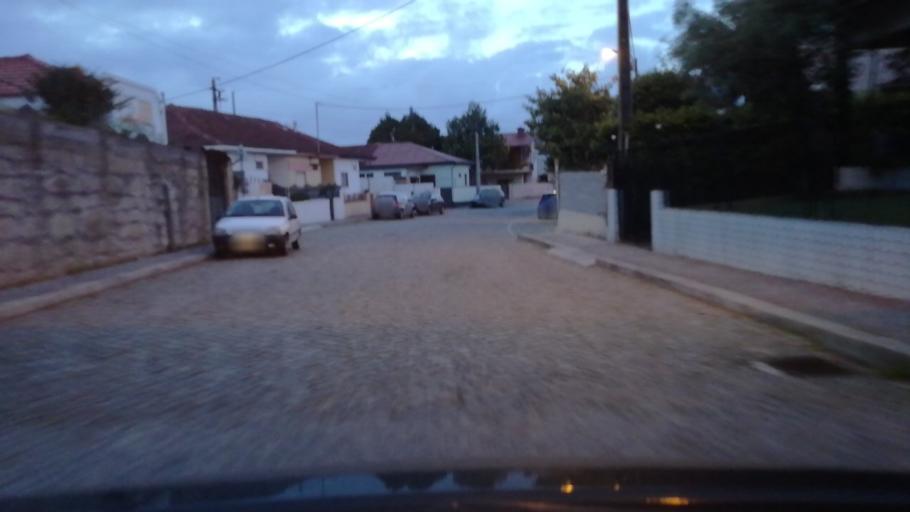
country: PT
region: Porto
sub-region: Maia
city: Anta
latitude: 41.2614
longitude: -8.6085
